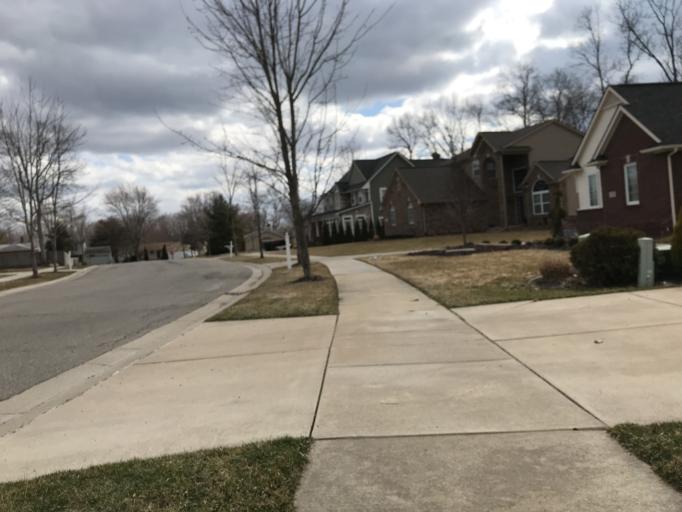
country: US
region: Michigan
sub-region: Oakland County
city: South Lyon
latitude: 42.4689
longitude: -83.6398
